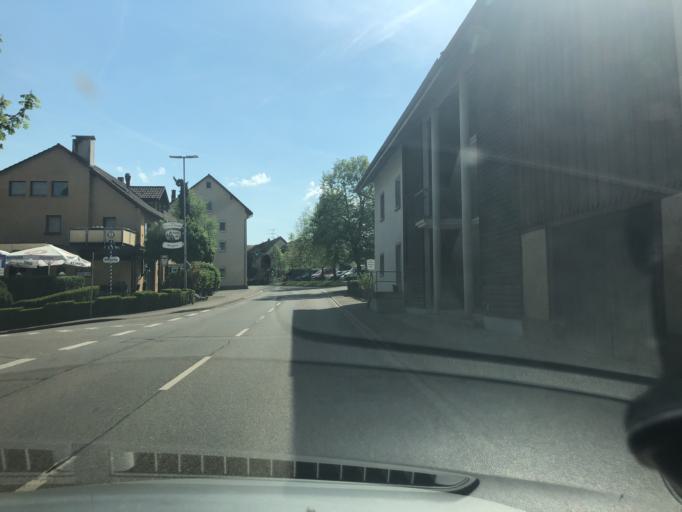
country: DE
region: Baden-Wuerttemberg
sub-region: Freiburg Region
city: Weilheim
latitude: 47.6435
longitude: 8.2465
